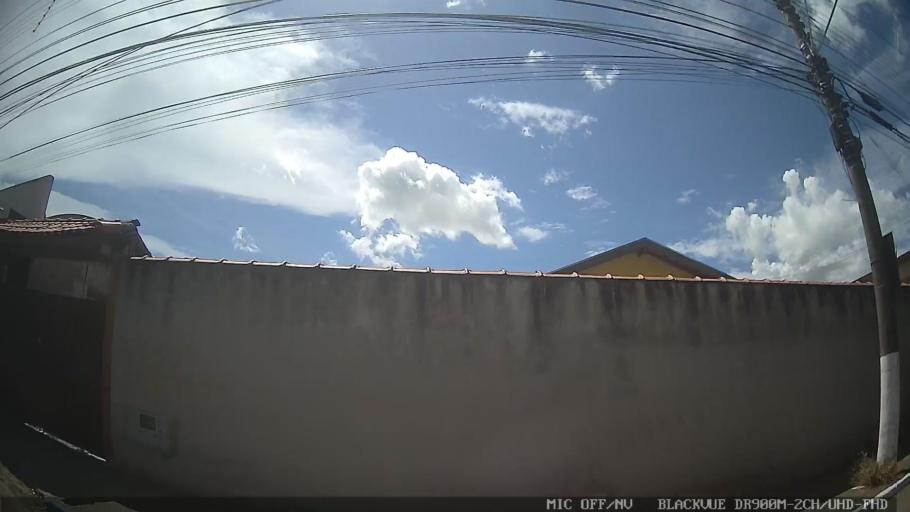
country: BR
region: Sao Paulo
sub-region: Conchas
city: Conchas
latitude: -23.0281
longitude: -48.0155
